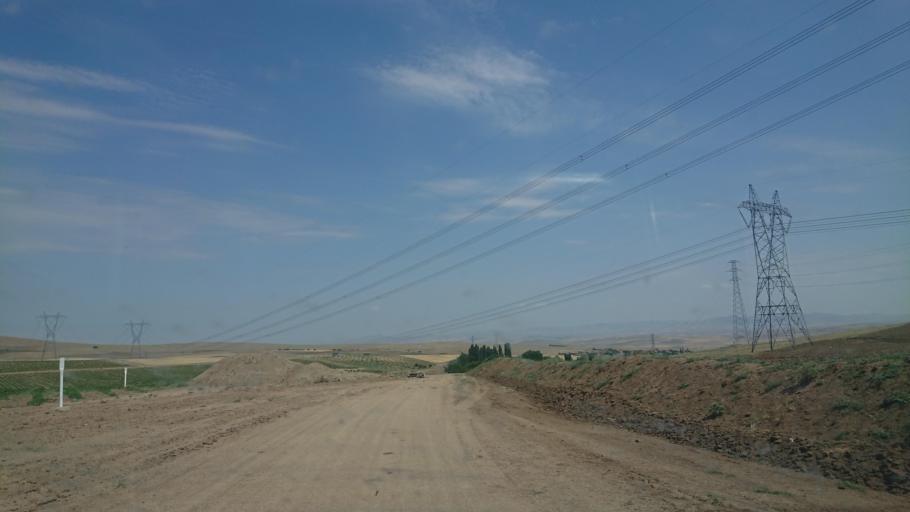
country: TR
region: Aksaray
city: Agacoren
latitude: 38.9012
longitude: 33.9243
